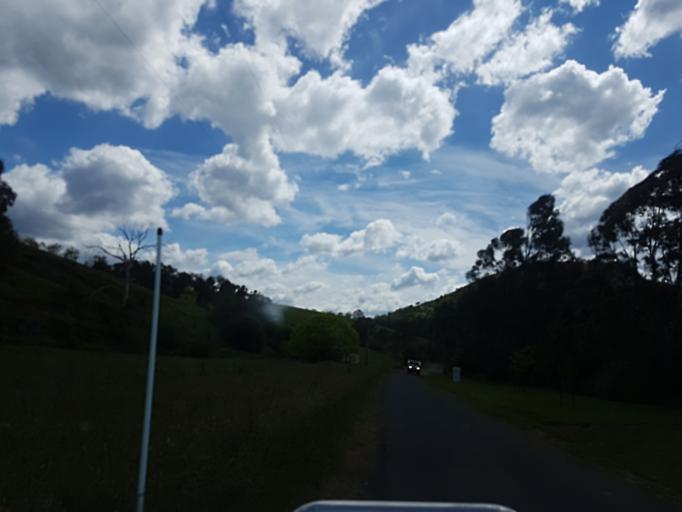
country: AU
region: Victoria
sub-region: East Gippsland
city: Bairnsdale
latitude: -37.4396
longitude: 147.2513
